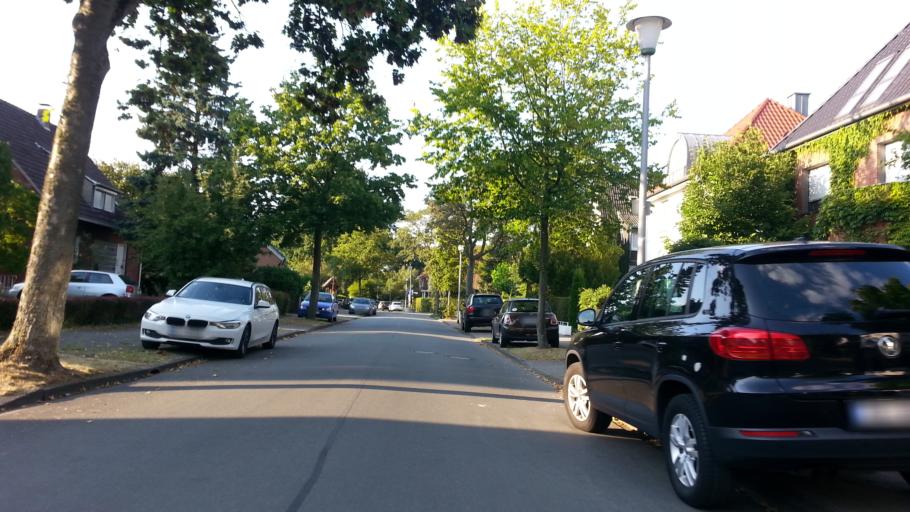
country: DE
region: North Rhine-Westphalia
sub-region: Regierungsbezirk Munster
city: Muenster
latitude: 51.9763
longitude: 7.6287
